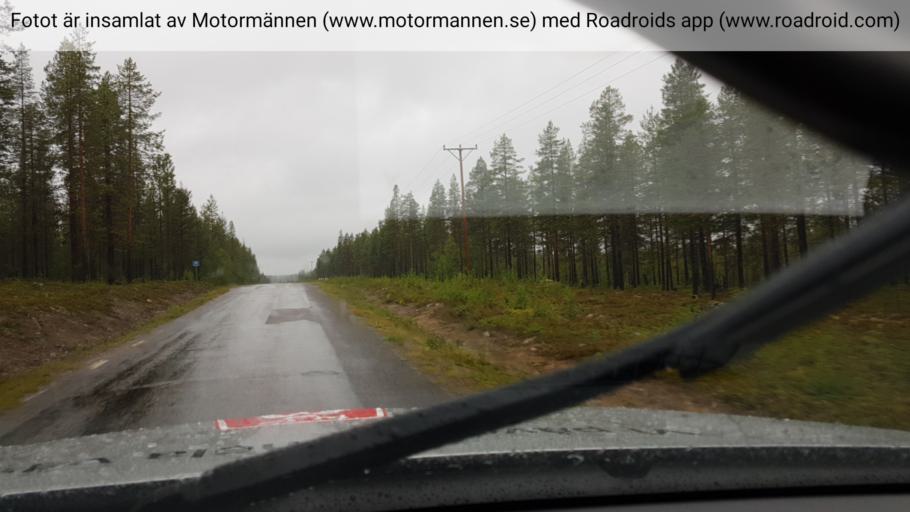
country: SE
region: Norrbotten
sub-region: Jokkmokks Kommun
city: Jokkmokk
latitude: 66.5949
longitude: 19.4737
